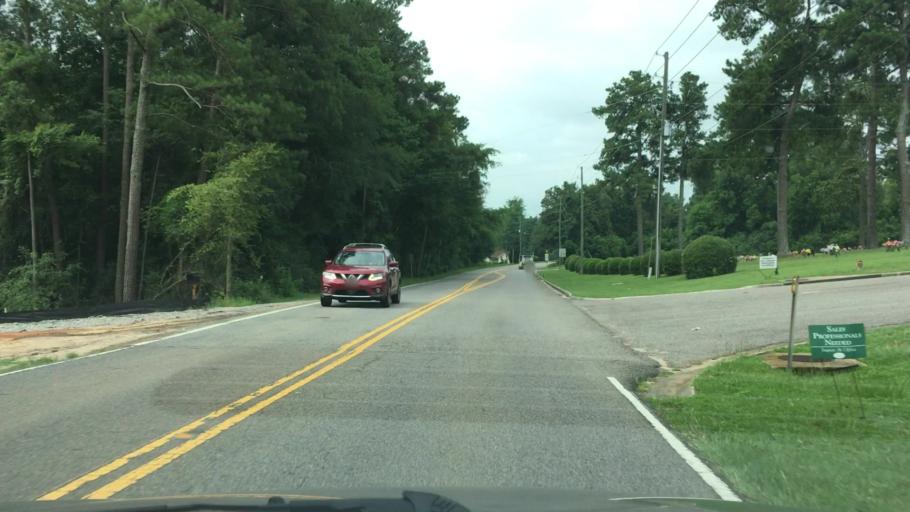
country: US
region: South Carolina
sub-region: Aiken County
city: Belvedere
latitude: 33.5459
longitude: -81.9586
